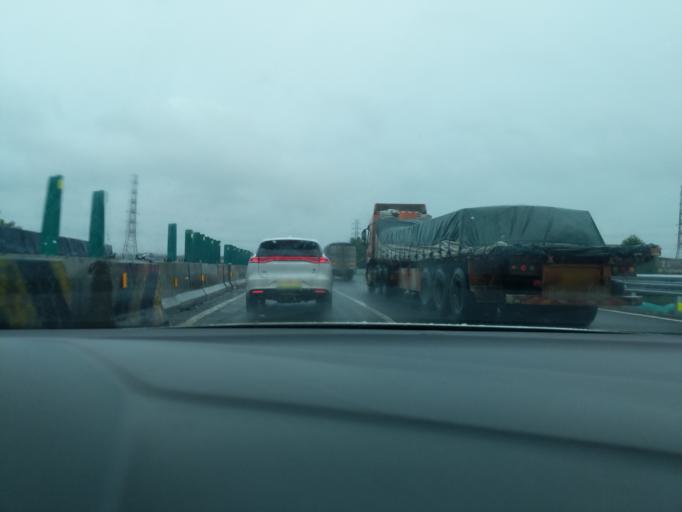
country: CN
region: Guangdong
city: Shuikou
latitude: 22.4694
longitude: 112.7583
